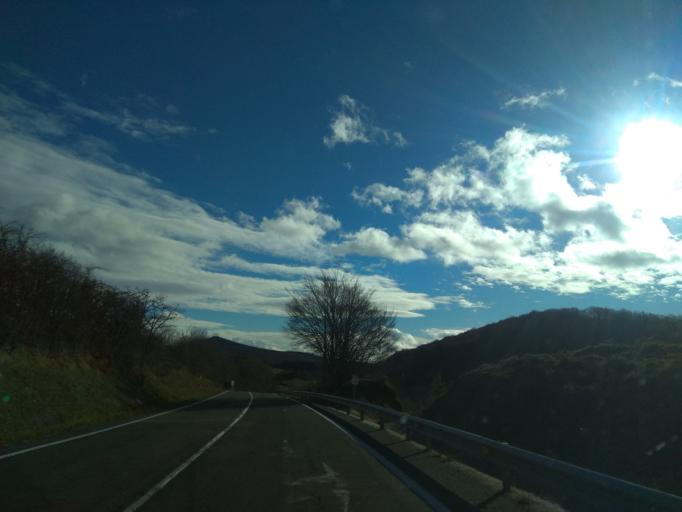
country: ES
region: Cantabria
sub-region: Provincia de Cantabria
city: San Martin de Elines
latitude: 42.9325
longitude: -3.8285
